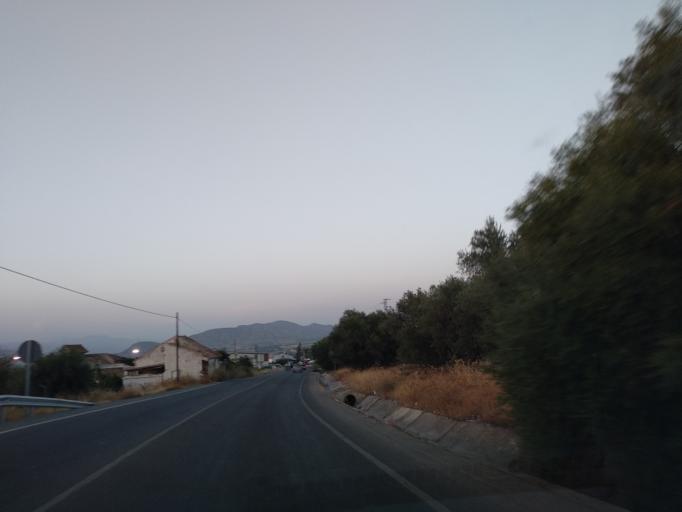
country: ES
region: Andalusia
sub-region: Provincia de Malaga
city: Alhaurin el Grande
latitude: 36.6539
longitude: -4.6788
